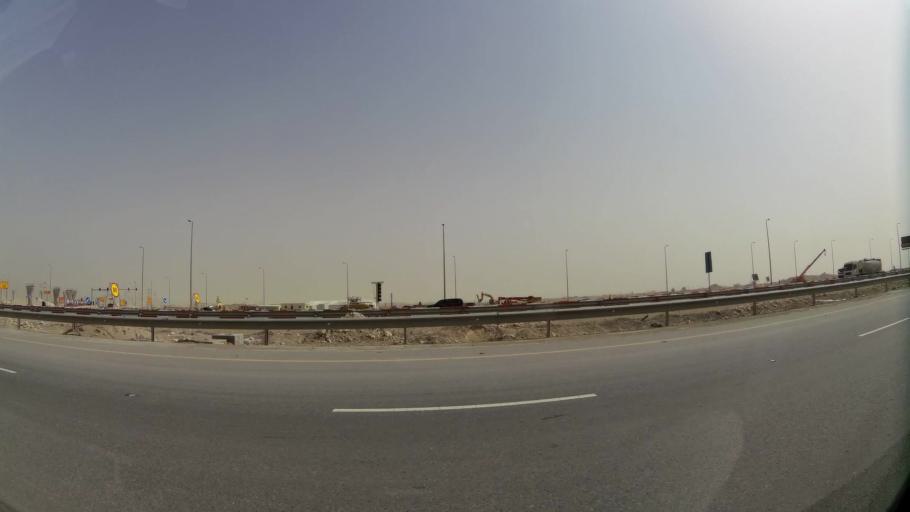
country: QA
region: Baladiyat ar Rayyan
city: Ar Rayyan
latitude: 25.1711
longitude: 51.3225
